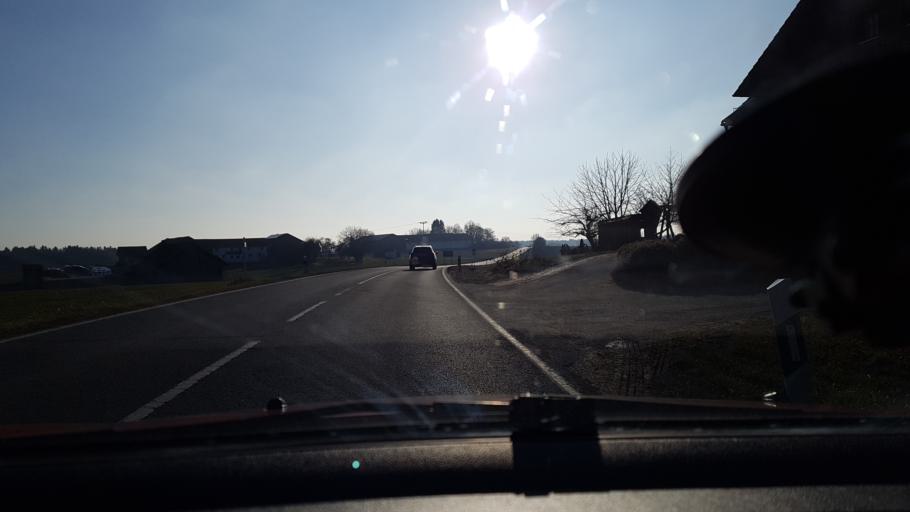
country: DE
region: Bavaria
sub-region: Lower Bavaria
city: Wittibreut
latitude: 48.3383
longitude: 12.9575
